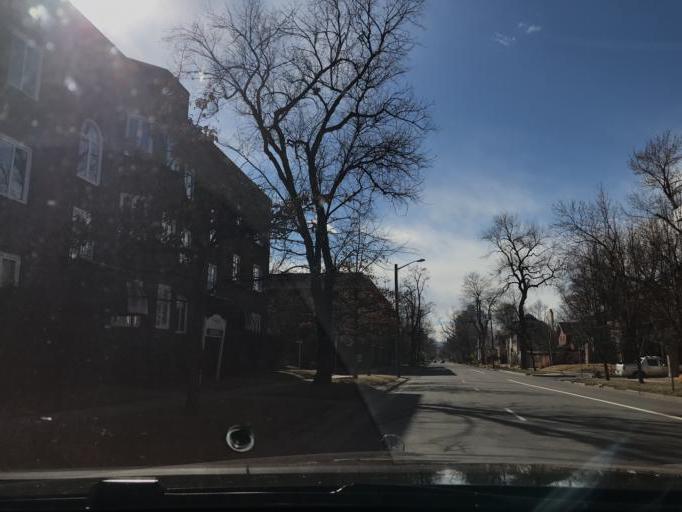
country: US
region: Colorado
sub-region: Denver County
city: Denver
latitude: 39.7291
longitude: -104.9688
